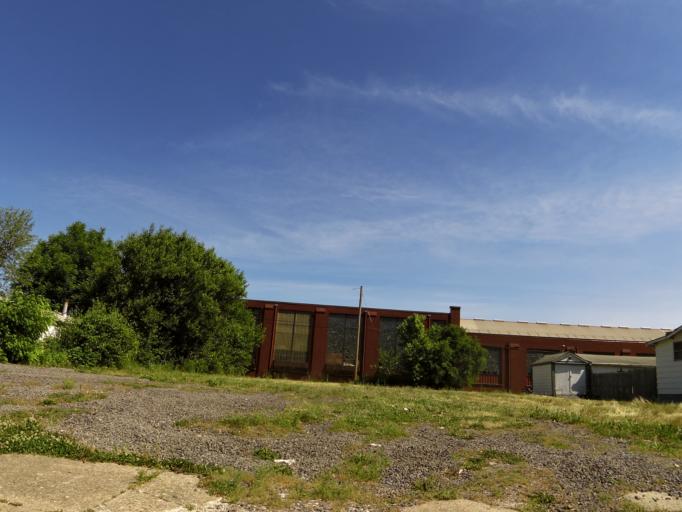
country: US
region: Illinois
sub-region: Vermilion County
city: Danville
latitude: 40.1350
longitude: -87.5855
